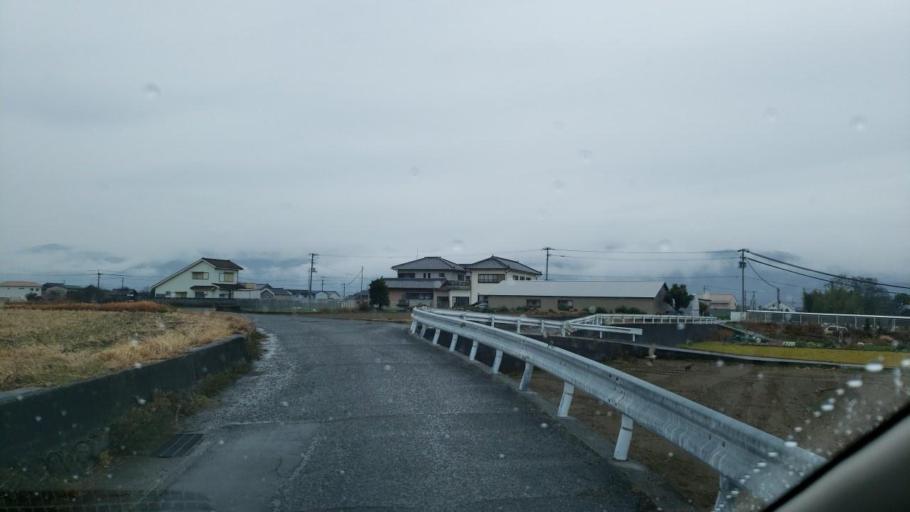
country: JP
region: Tokushima
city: Kamojimacho-jogejima
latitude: 34.0830
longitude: 134.2564
